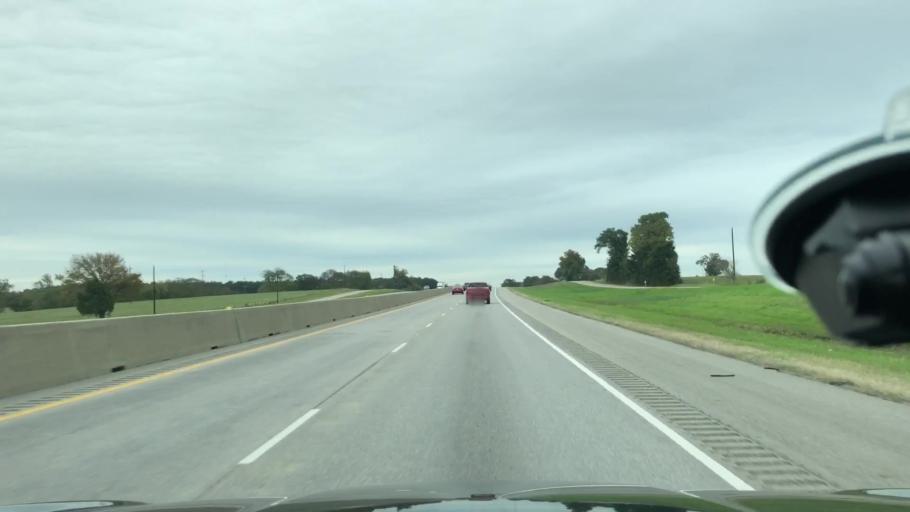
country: US
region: Texas
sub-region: Franklin County
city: Mount Vernon
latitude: 33.1622
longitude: -95.1587
